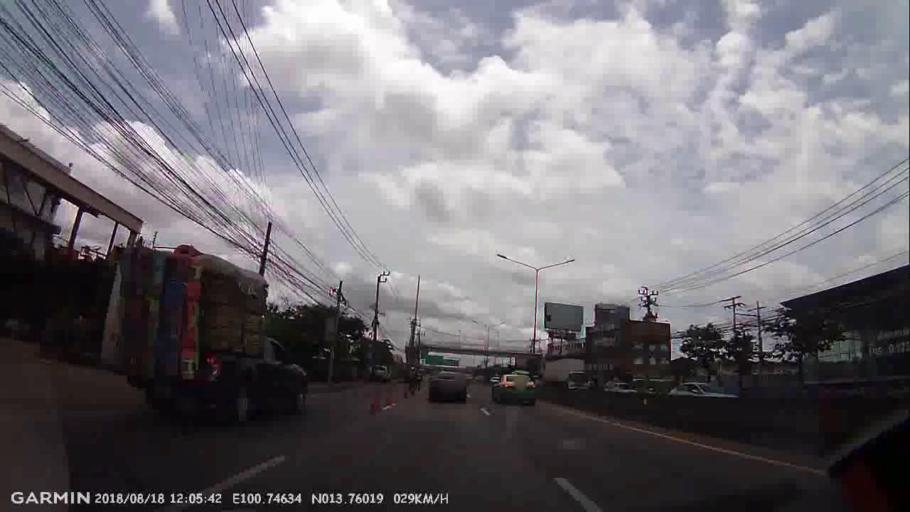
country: TH
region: Bangkok
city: Lat Krabang
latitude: 13.7601
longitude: 100.7463
